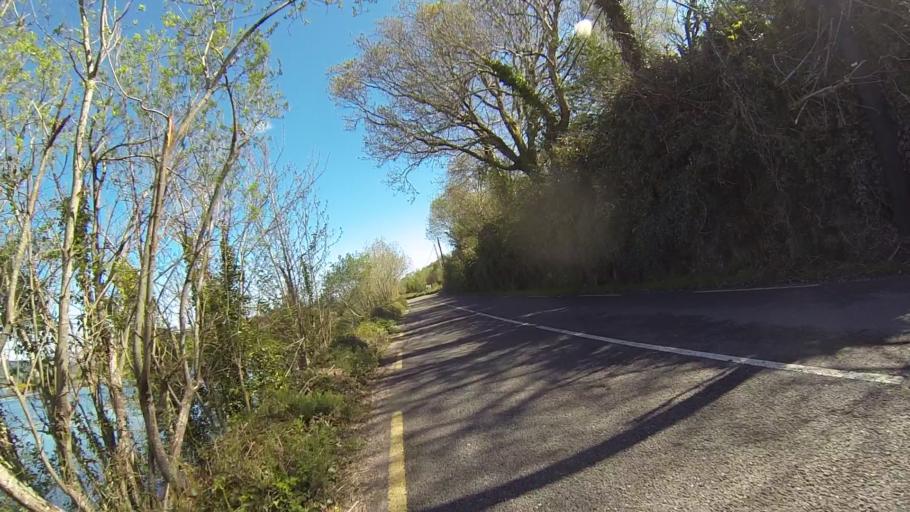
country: IE
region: Munster
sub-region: Ciarrai
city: Kenmare
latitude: 51.8455
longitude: -9.6436
